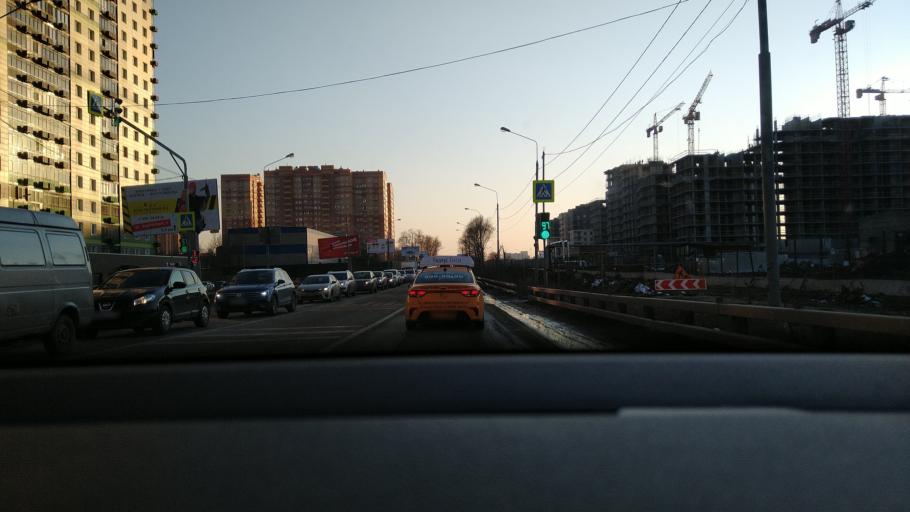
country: RU
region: Moscow
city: Khimki
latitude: 55.8675
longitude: 37.3952
